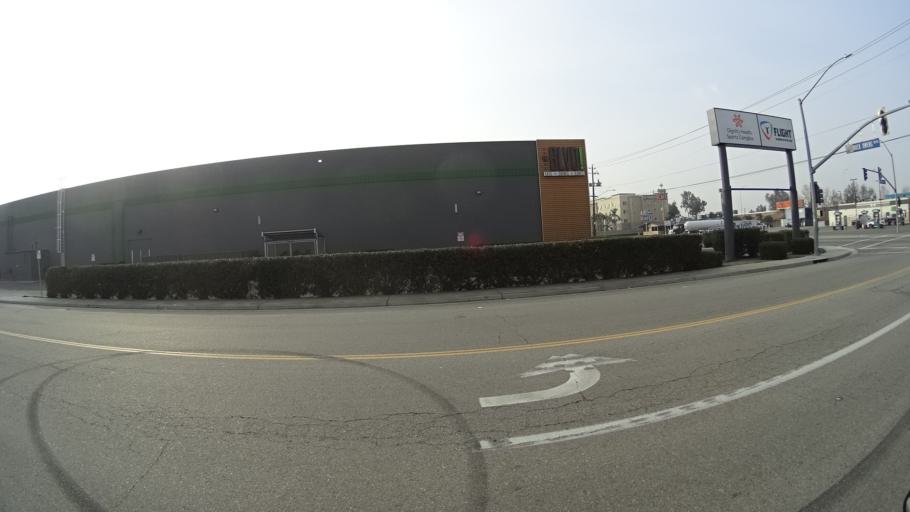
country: US
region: California
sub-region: Kern County
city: Bakersfield
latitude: 35.3895
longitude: -119.0427
